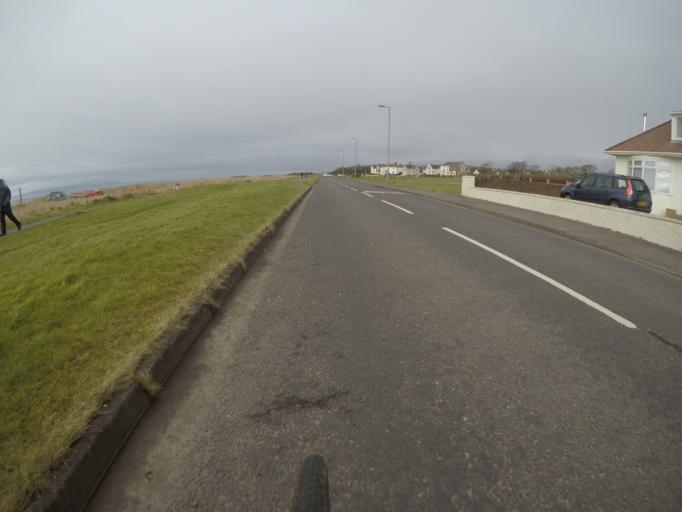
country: GB
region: Scotland
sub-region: North Ayrshire
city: Ardrossan
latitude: 55.6504
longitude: -4.8173
